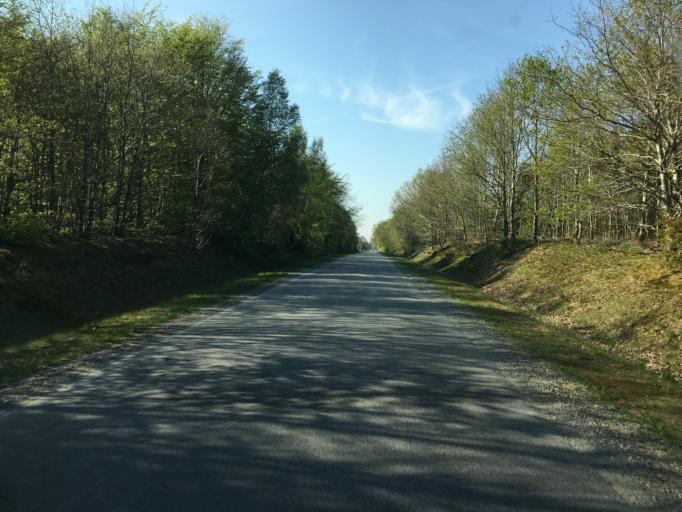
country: DK
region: South Denmark
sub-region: Haderslev Kommune
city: Vojens
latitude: 55.2416
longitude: 9.3204
